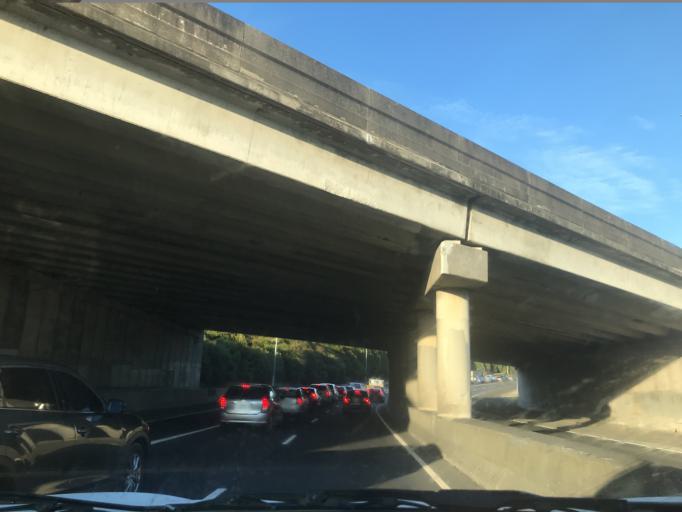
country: NZ
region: Auckland
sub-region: Auckland
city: Tamaki
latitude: -36.9167
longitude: 174.8345
